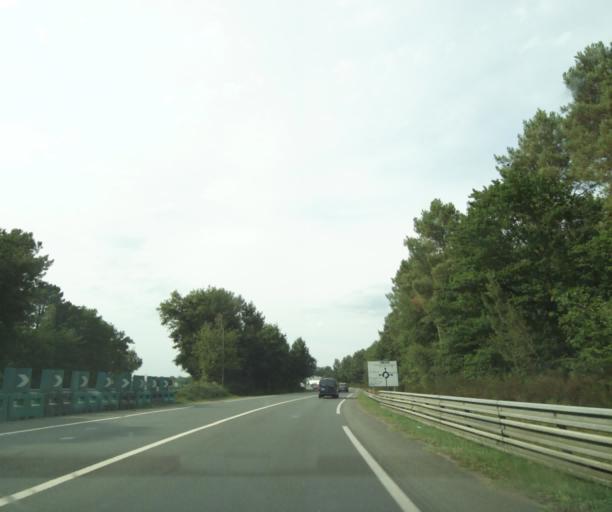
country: FR
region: Pays de la Loire
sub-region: Departement de la Sarthe
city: Mulsanne
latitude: 47.9391
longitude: 0.2363
